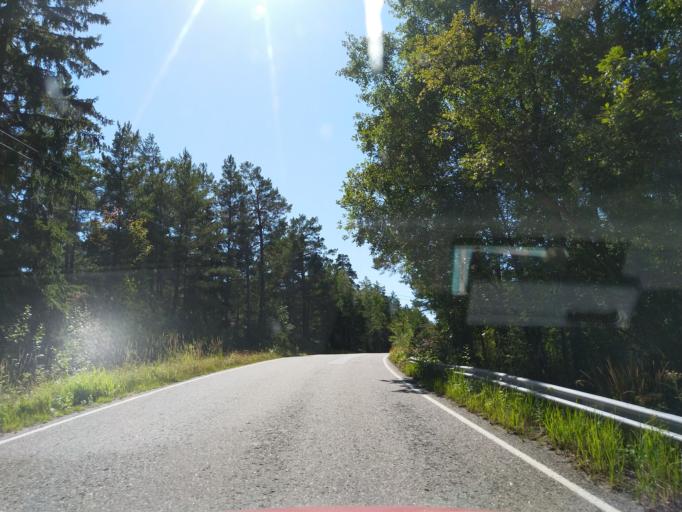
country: FI
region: Varsinais-Suomi
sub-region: Aboland-Turunmaa
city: Dragsfjaerd
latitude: 60.0170
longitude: 22.4772
